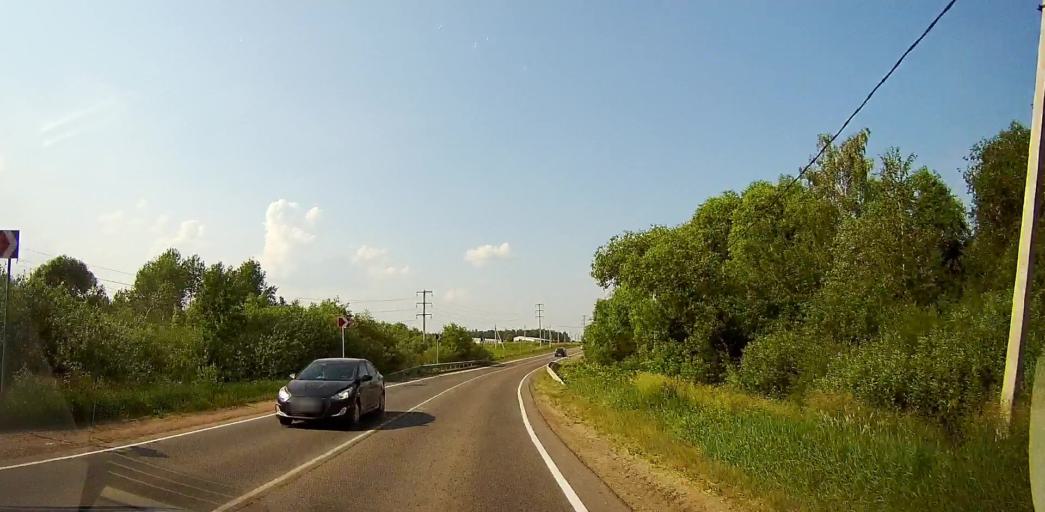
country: RU
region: Moskovskaya
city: Barybino
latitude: 55.3006
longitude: 37.9105
